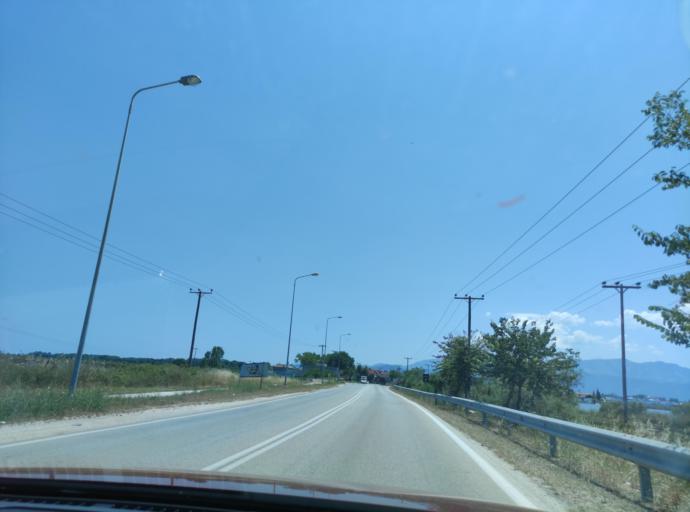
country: GR
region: East Macedonia and Thrace
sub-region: Nomos Kavalas
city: Keramoti
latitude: 40.8666
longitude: 24.7051
